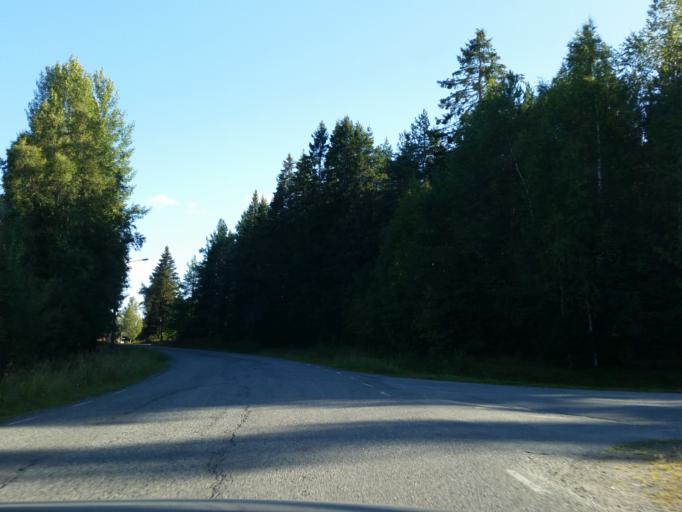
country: SE
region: Vaesterbotten
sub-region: Robertsfors Kommun
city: Robertsfors
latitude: 64.0552
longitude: 20.8537
